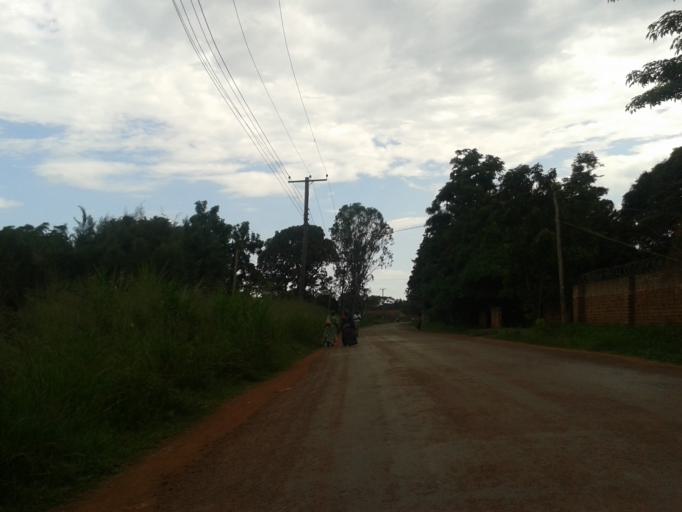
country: UG
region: Northern Region
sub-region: Gulu District
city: Gulu
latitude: 2.7826
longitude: 32.3061
